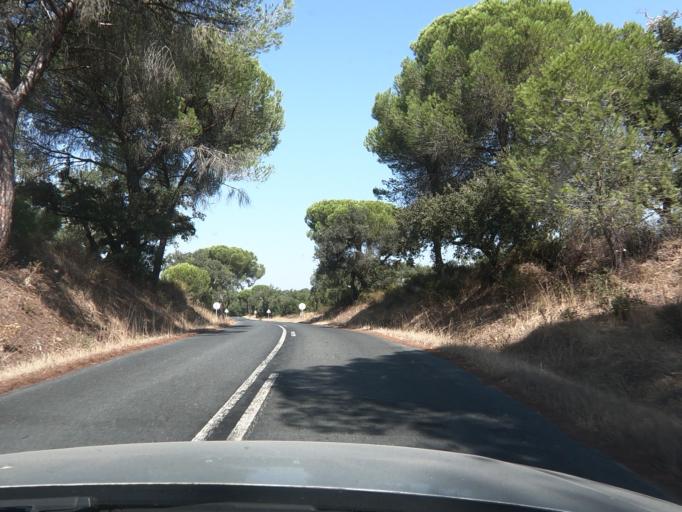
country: PT
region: Setubal
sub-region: Alcacer do Sal
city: Alcacer do Sal
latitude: 38.2980
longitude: -8.4043
